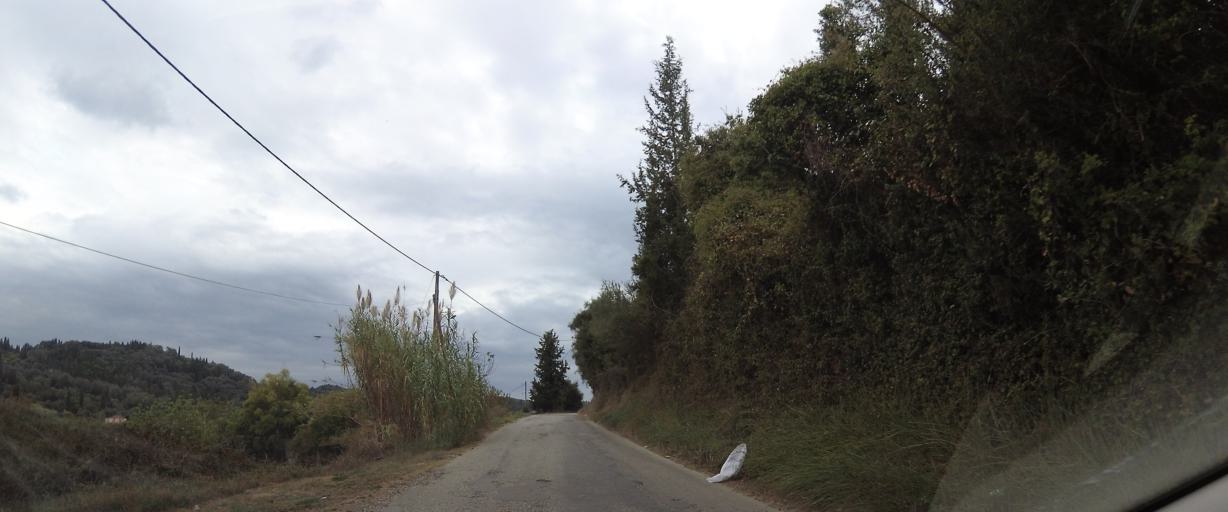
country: GR
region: Ionian Islands
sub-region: Nomos Kerkyras
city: Agios Georgis
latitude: 39.7571
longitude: 19.6891
